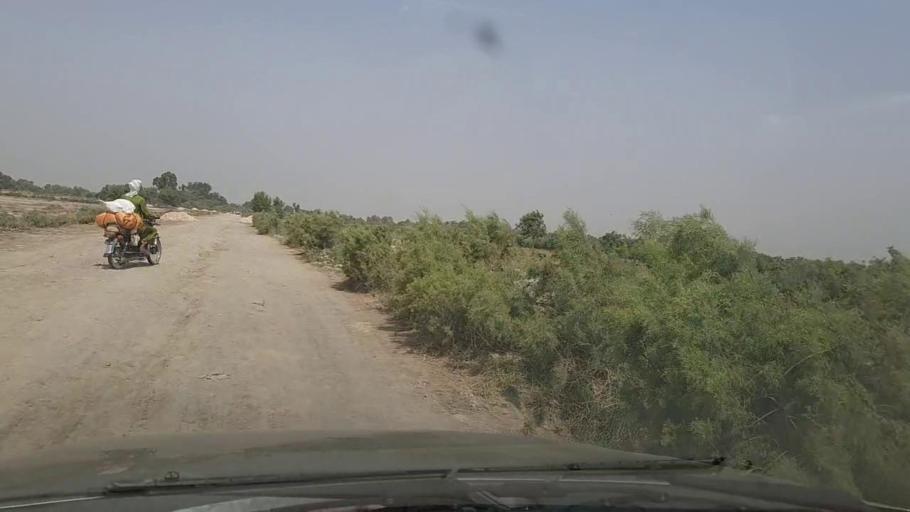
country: PK
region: Sindh
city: Thul
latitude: 28.3981
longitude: 68.7111
